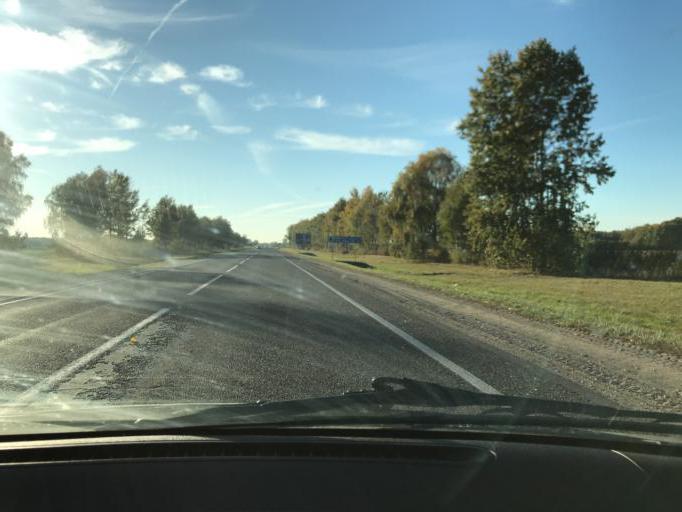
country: BY
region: Brest
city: Horad Kobryn
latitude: 52.2192
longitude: 24.4401
